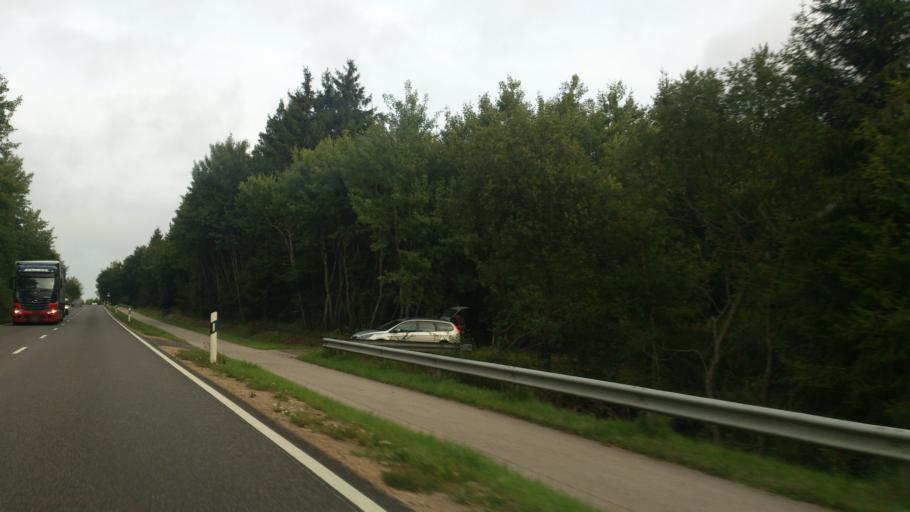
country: DE
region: Rheinland-Pfalz
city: Ohlenhard
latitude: 50.4339
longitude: 6.7363
